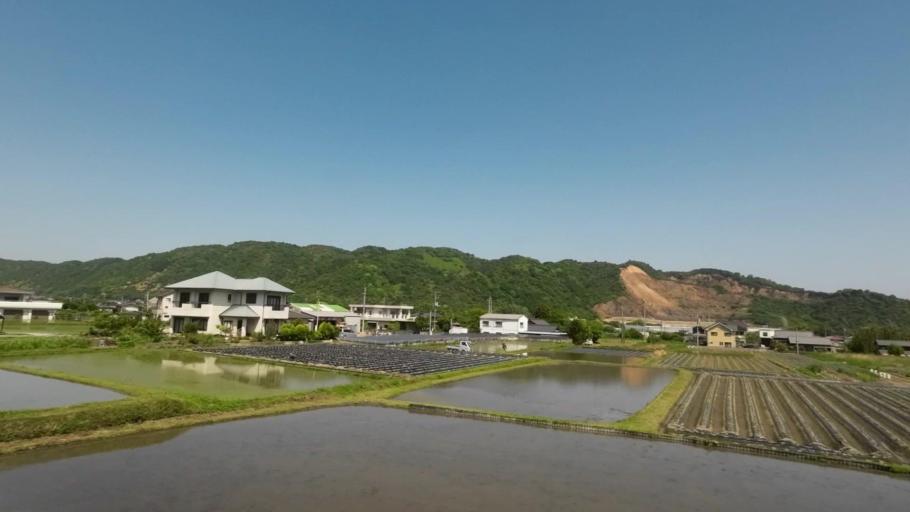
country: JP
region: Ehime
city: Niihama
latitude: 33.9564
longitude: 133.4185
